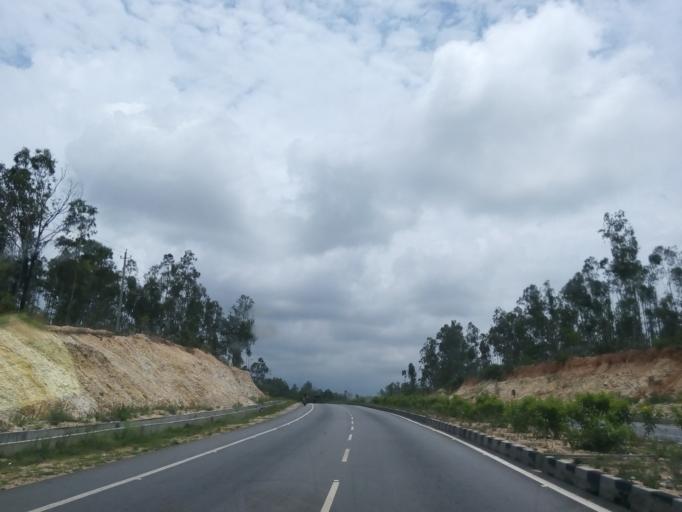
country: IN
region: Karnataka
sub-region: Hassan
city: Hassan
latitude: 12.9924
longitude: 76.1788
